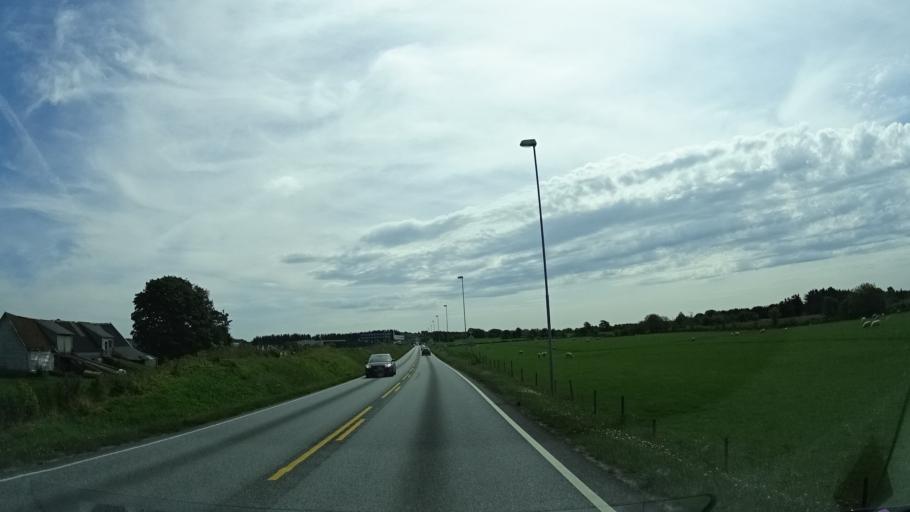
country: NO
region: Rogaland
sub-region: Randaberg
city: Randaberg
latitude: 58.9996
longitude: 5.6459
